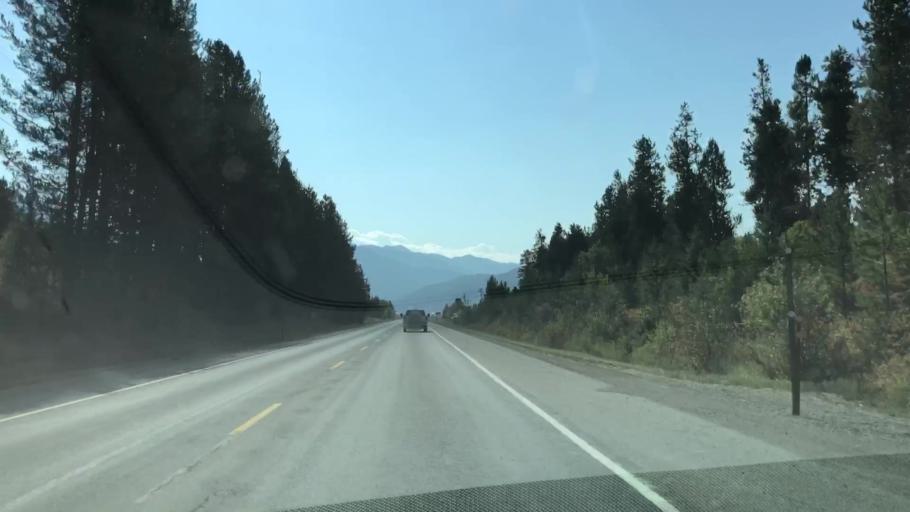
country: US
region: Wyoming
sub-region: Teton County
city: Hoback
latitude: 43.1970
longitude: -111.0408
